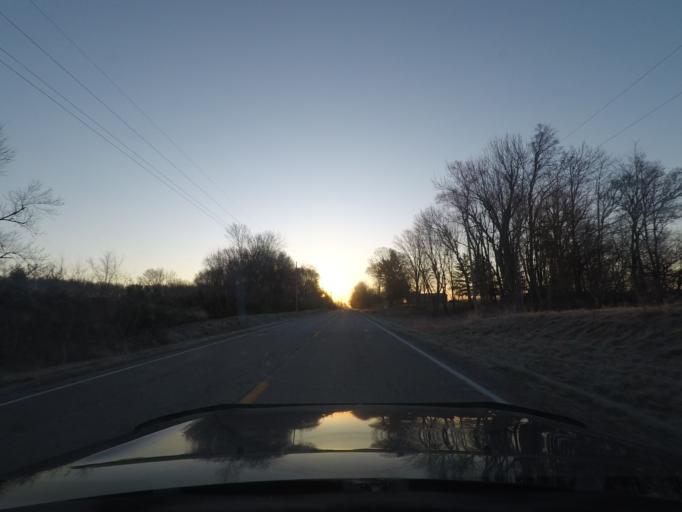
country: US
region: Indiana
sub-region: Saint Joseph County
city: Walkerton
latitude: 41.4480
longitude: -86.4227
